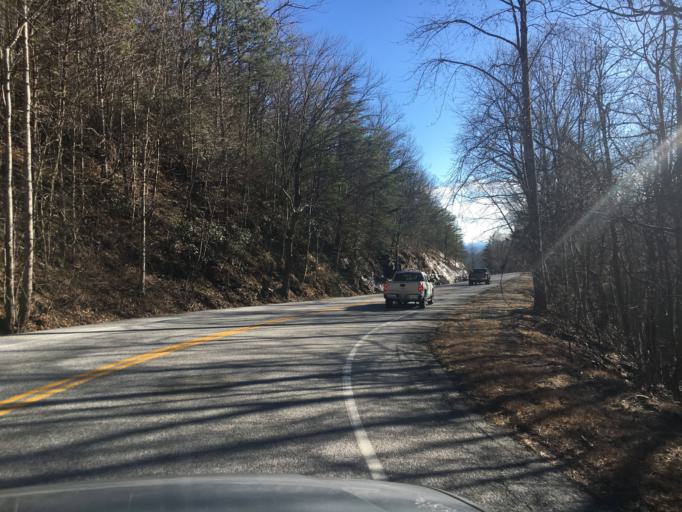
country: US
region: Georgia
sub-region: Union County
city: Blairsville
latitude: 34.7263
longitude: -83.9130
